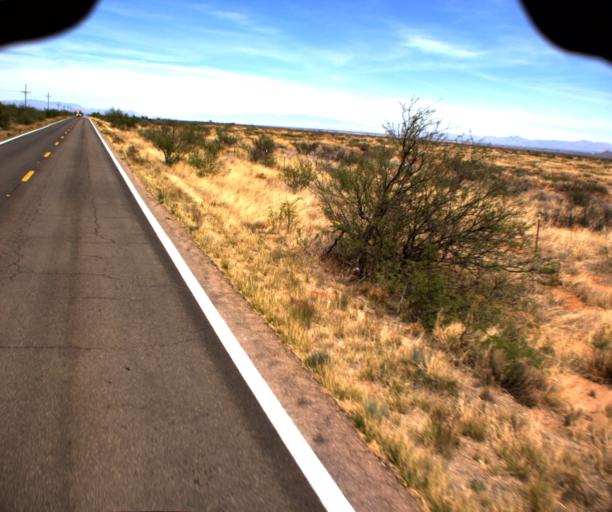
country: US
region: Arizona
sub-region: Cochise County
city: Tombstone
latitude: 31.9143
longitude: -109.8179
